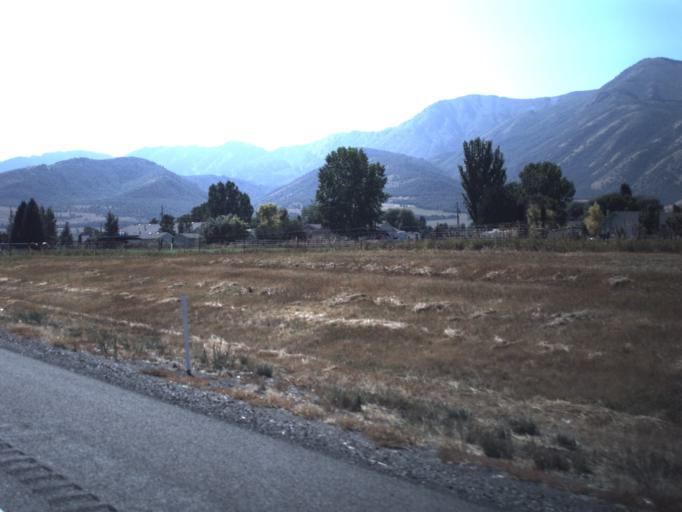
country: US
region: Utah
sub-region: Cache County
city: Wellsville
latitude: 41.6365
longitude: -111.9197
